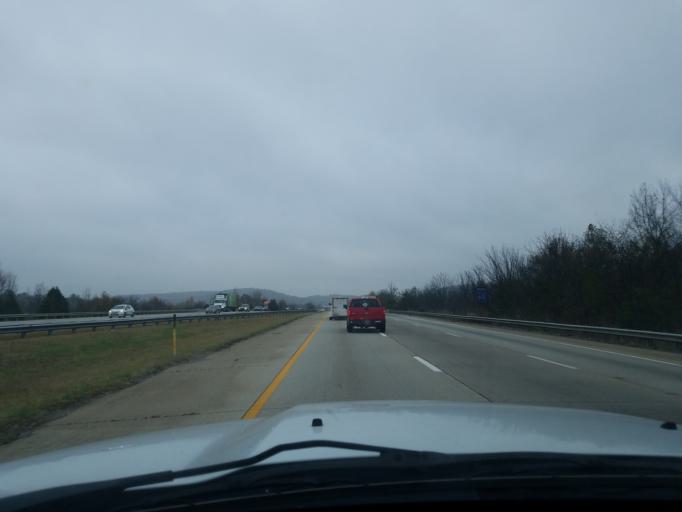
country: US
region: Kentucky
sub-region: Bullitt County
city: Shepherdsville
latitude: 37.9331
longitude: -85.6880
